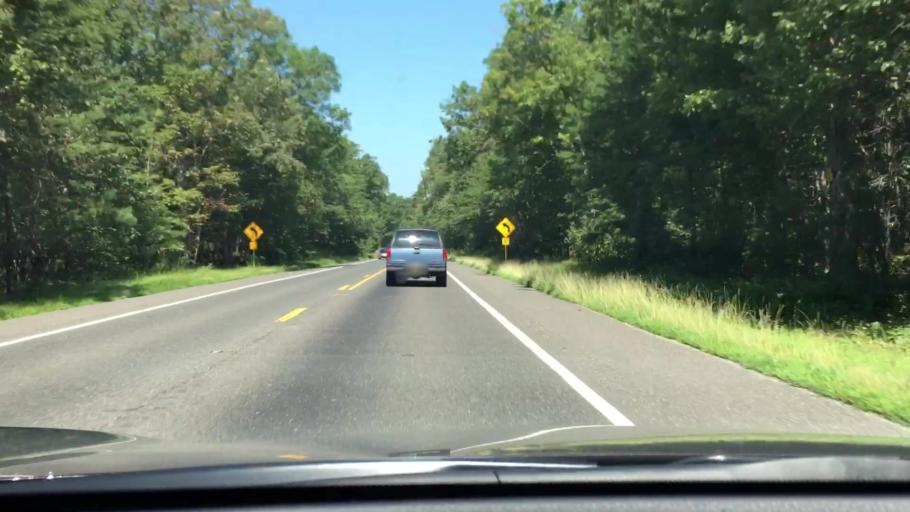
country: US
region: New Jersey
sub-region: Cumberland County
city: Port Norris
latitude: 39.2825
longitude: -74.9503
